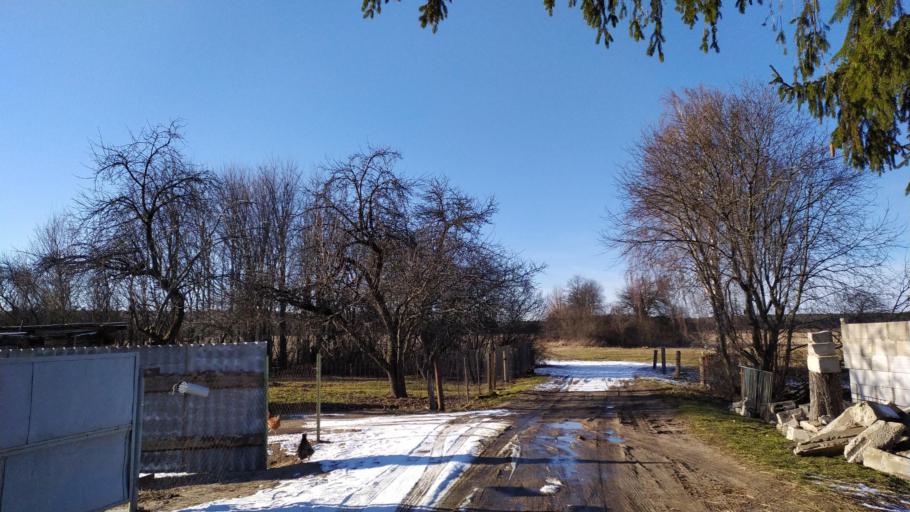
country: BY
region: Brest
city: Kamyanyets
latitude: 52.3753
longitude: 23.8830
